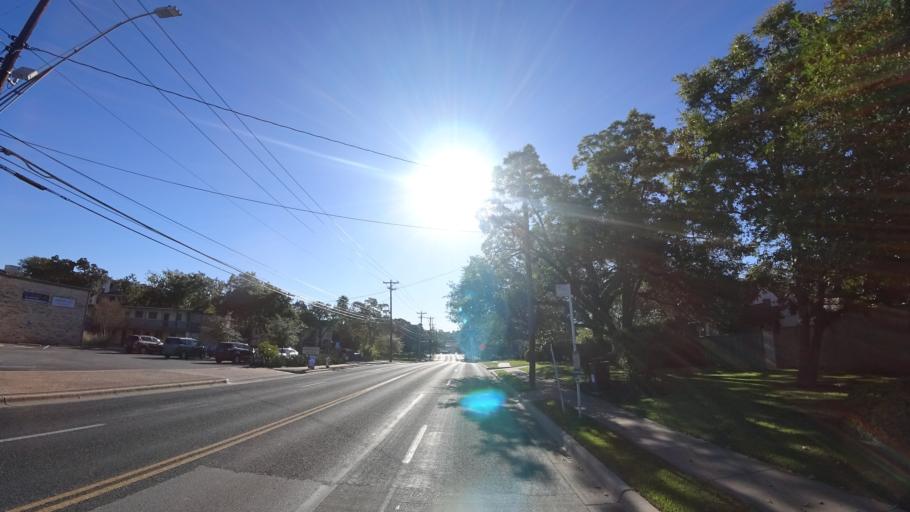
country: US
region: Texas
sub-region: Travis County
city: Rollingwood
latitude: 30.2875
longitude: -97.7669
